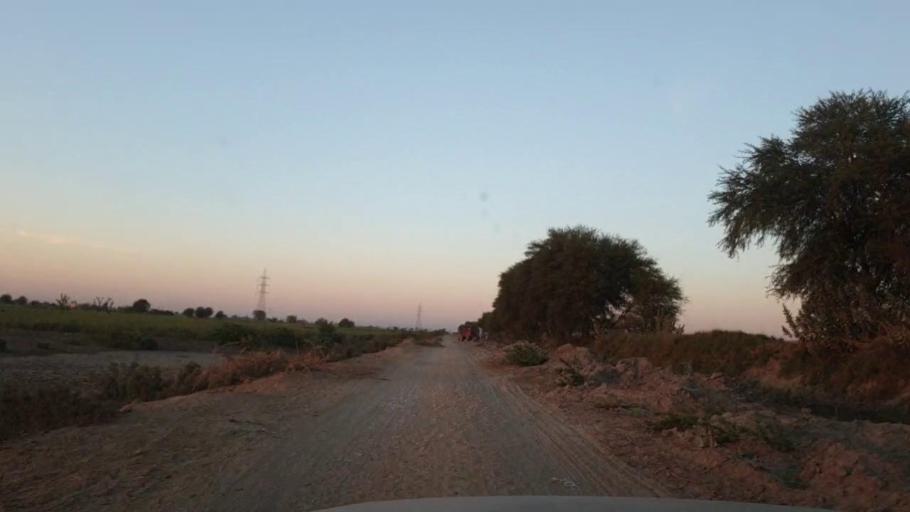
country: PK
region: Sindh
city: Kunri
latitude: 25.1478
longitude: 69.4460
